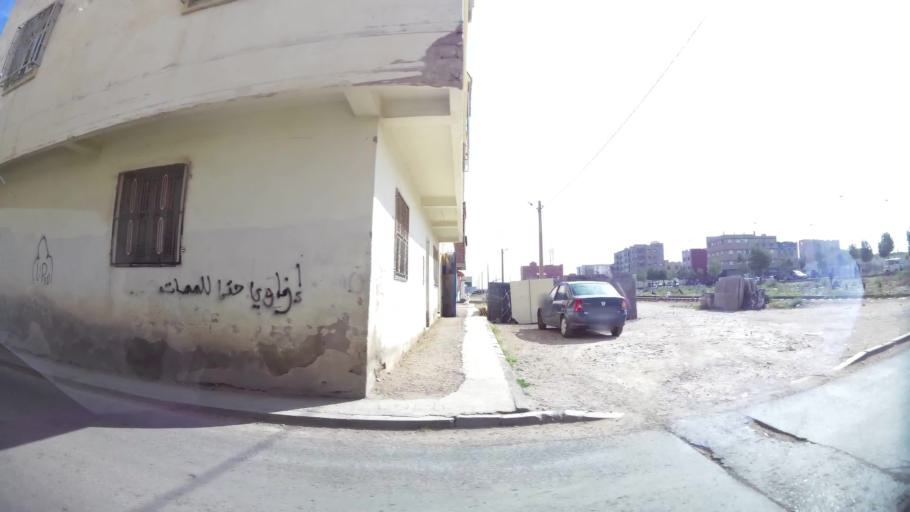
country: MA
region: Oriental
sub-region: Oujda-Angad
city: Oujda
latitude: 34.7123
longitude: -1.8866
